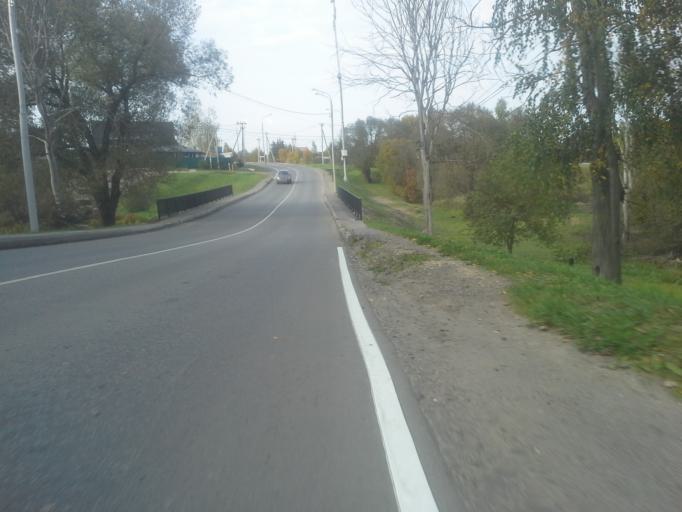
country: RU
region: Moskovskaya
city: Selyatino
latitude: 55.4290
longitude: 36.9617
